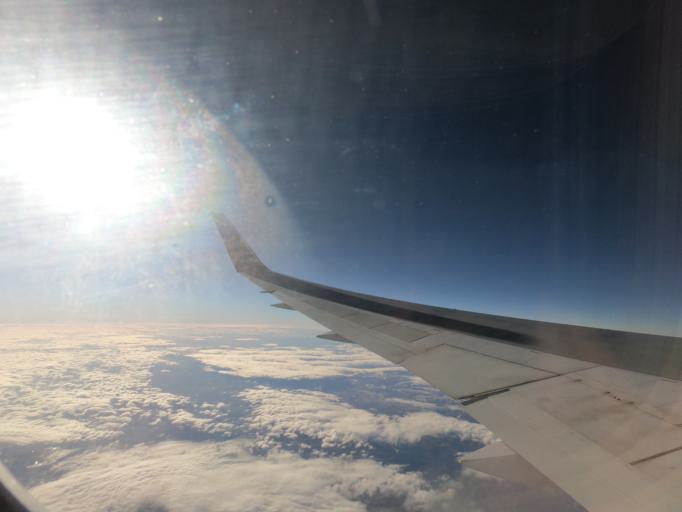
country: GB
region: England
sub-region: City and Borough of Wakefield
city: Castleford
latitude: 53.7072
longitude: -1.3507
